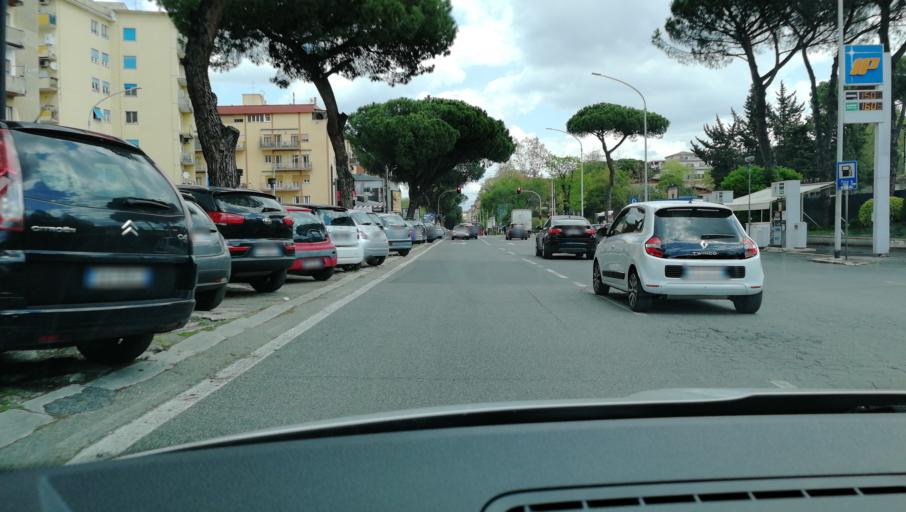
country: IT
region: Latium
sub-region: Citta metropolitana di Roma Capitale
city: Rome
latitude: 41.8467
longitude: 12.4869
